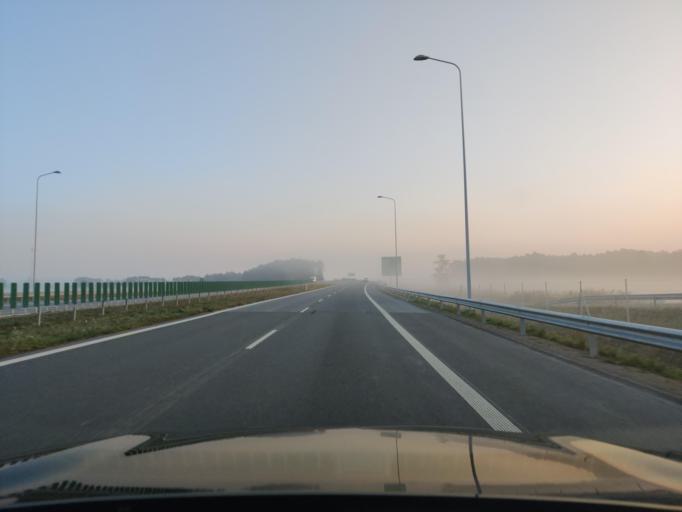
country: PL
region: Masovian Voivodeship
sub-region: Powiat mlawski
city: Strzegowo
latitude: 52.9358
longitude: 20.2890
